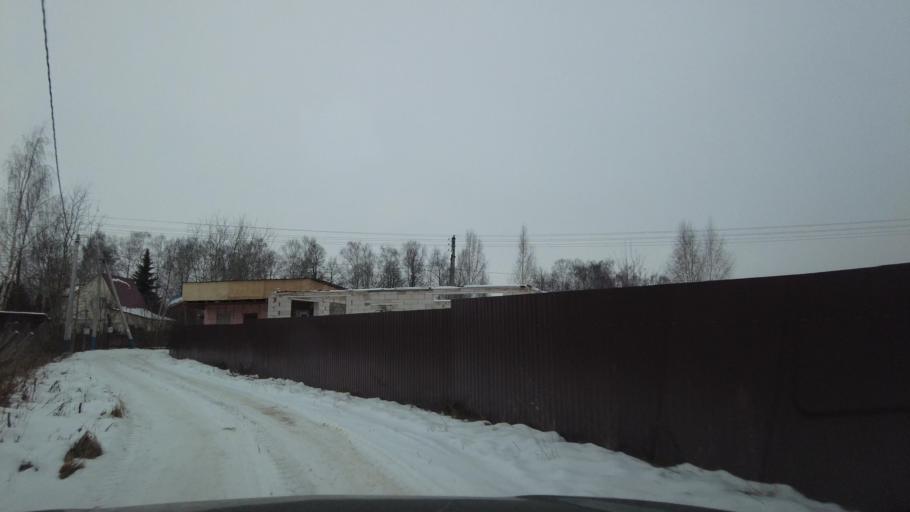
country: RU
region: Moskovskaya
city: Novopodrezkovo
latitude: 55.9870
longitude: 37.3916
